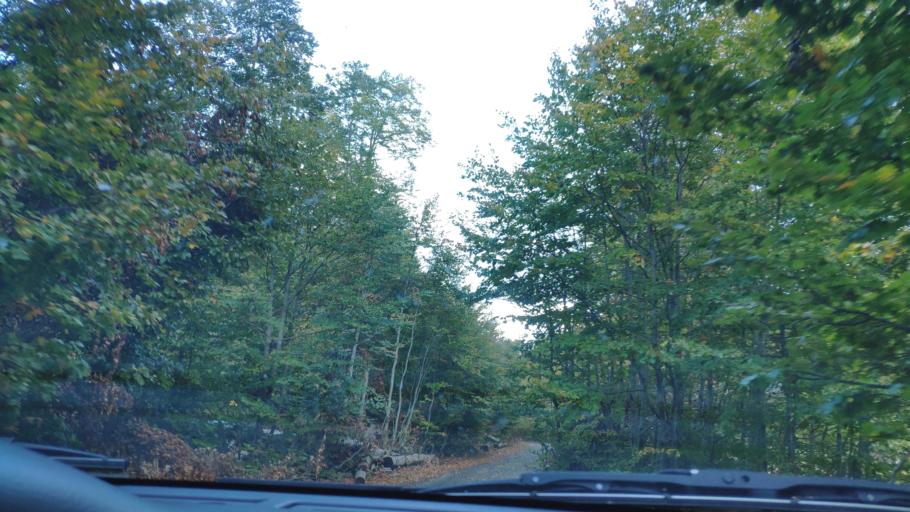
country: GR
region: West Macedonia
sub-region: Nomos Kastorias
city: Nestorio
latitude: 40.3097
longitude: 20.9154
